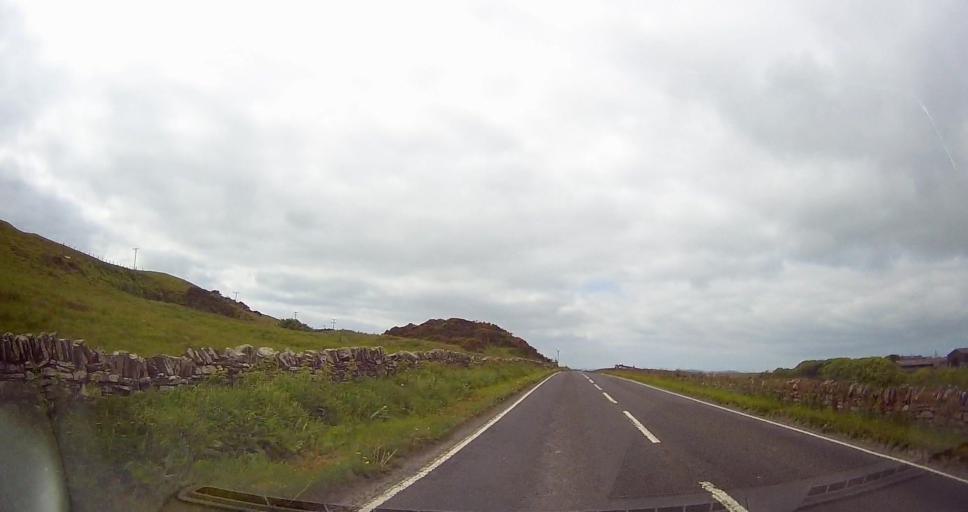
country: GB
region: Scotland
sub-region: Orkney Islands
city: Stromness
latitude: 59.0070
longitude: -3.1345
